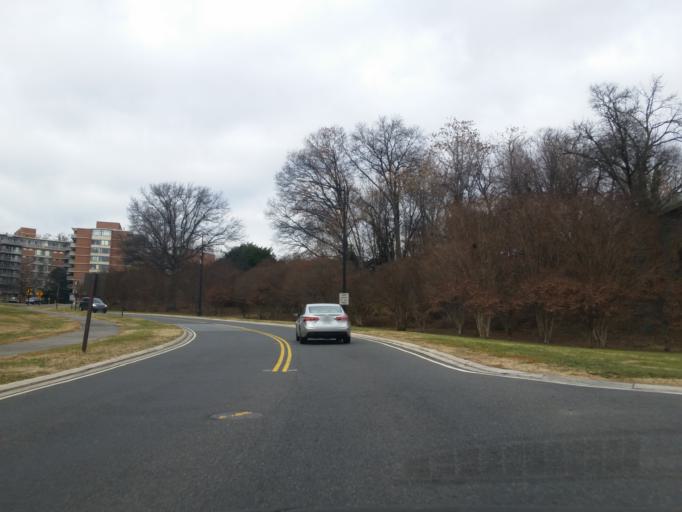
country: US
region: Washington, D.C.
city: Washington, D.C.
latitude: 38.9219
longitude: -77.0512
